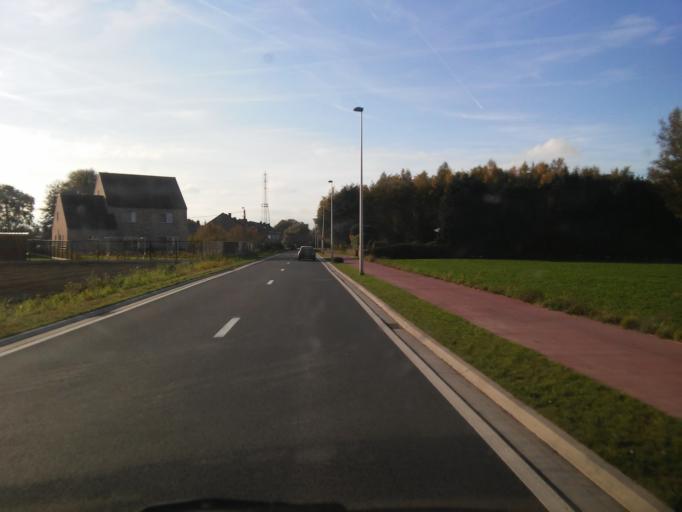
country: BE
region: Flanders
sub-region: Provincie Antwerpen
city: Sint-Katelijne-Waver
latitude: 51.0914
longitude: 4.5358
